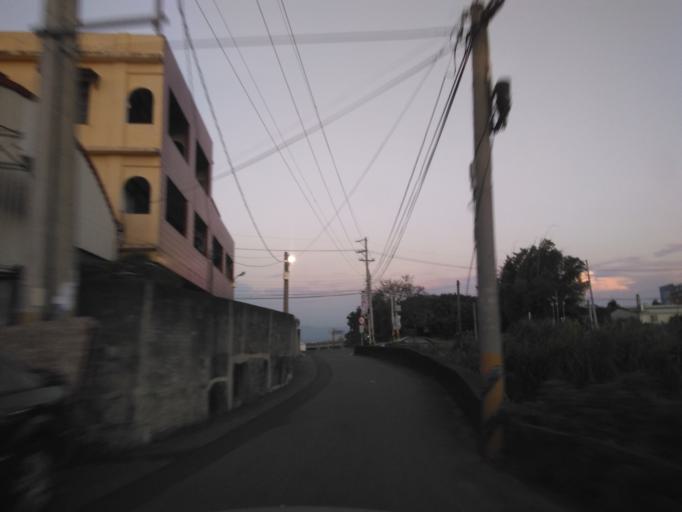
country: TW
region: Taiwan
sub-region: Changhua
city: Chang-hua
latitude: 24.0846
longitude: 120.5921
